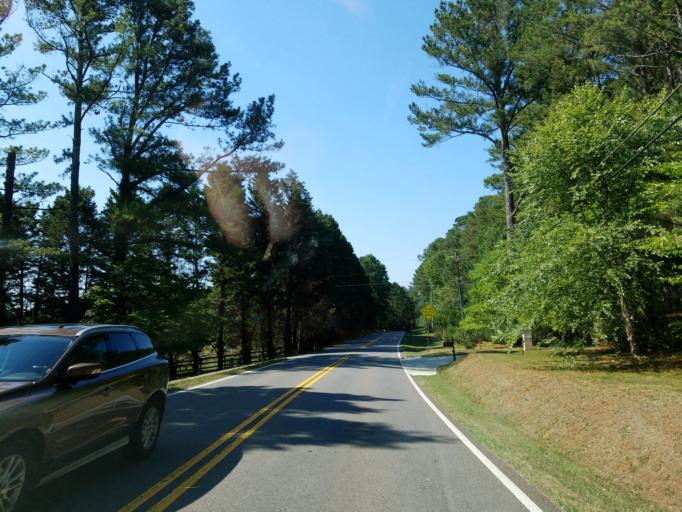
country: US
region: Georgia
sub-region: Fulton County
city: Milton
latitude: 34.1065
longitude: -84.3419
